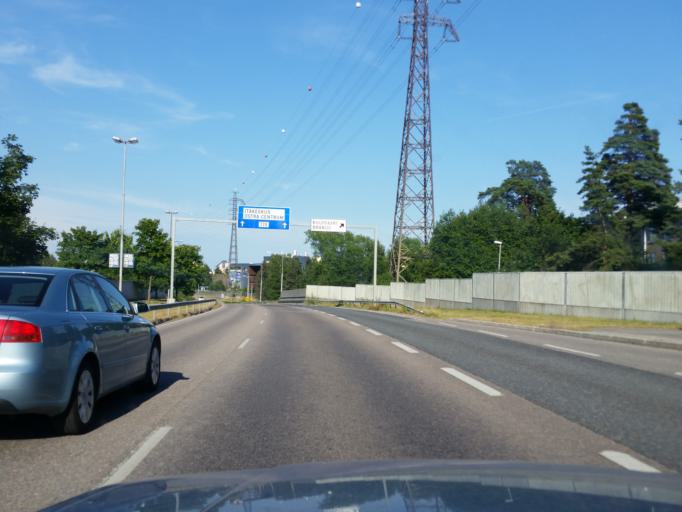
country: FI
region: Uusimaa
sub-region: Helsinki
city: Helsinki
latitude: 60.1887
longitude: 25.0113
